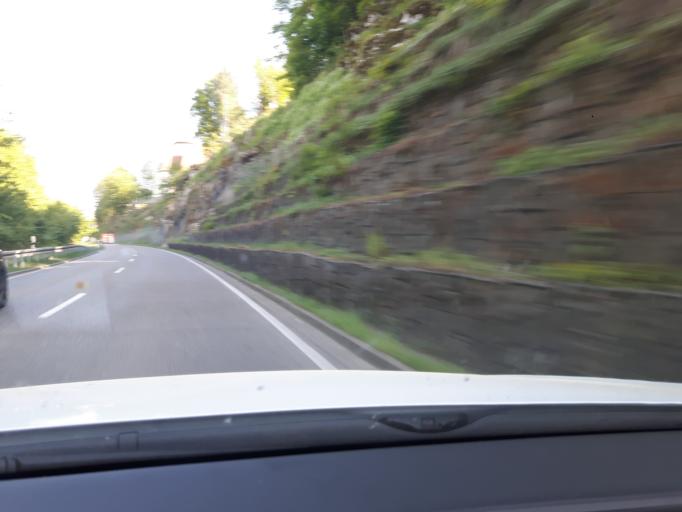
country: DE
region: Baden-Wuerttemberg
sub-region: Tuebingen Region
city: Pfullingen
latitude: 48.4284
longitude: 9.2720
